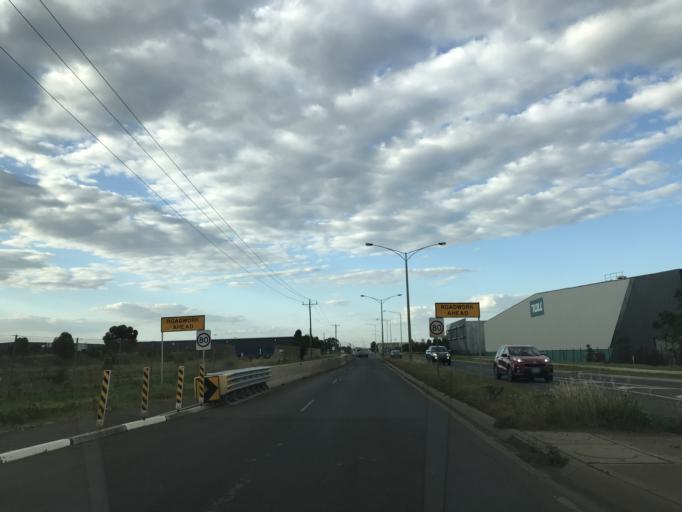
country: AU
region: Victoria
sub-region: Wyndham
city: Truganina
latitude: -37.8159
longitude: 144.7502
